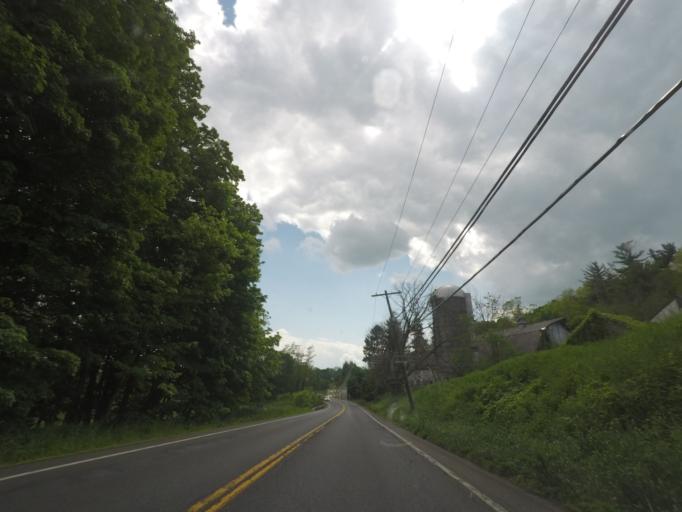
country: US
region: New York
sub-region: Dutchess County
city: Dover Plains
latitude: 41.8762
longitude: -73.5355
